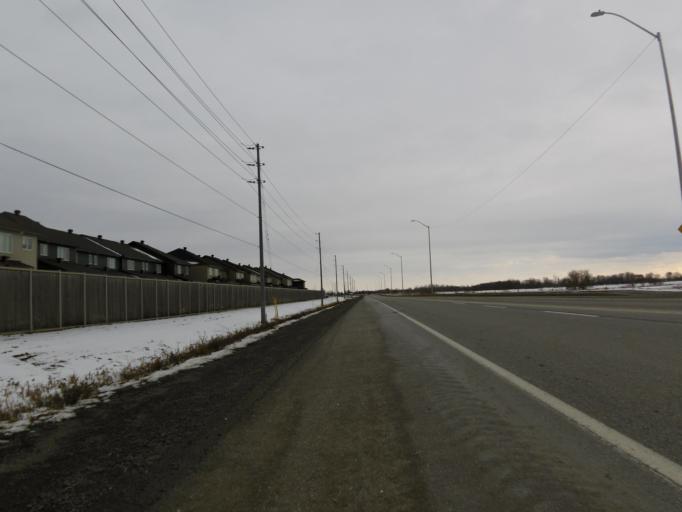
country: CA
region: Ontario
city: Bells Corners
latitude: 45.2734
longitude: -75.8677
